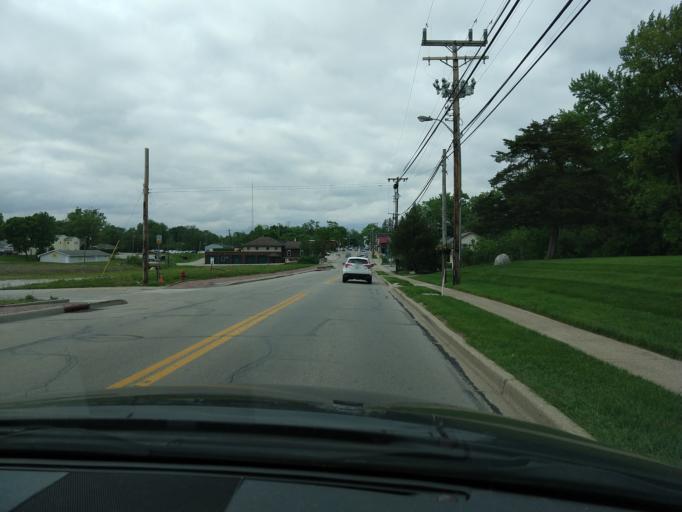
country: US
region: Indiana
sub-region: Hamilton County
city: Westfield
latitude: 40.0404
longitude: -86.1277
